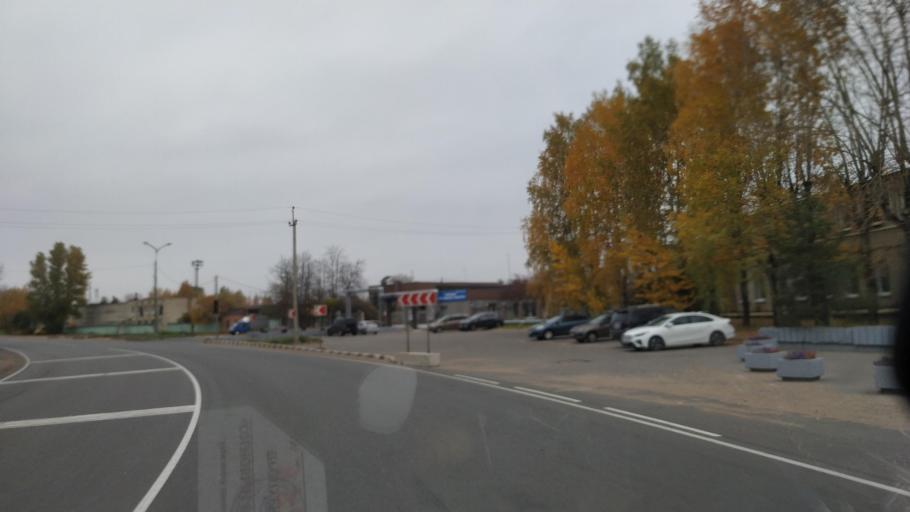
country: RU
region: Leningrad
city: Sosnovyy Bor
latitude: 59.8770
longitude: 29.0930
